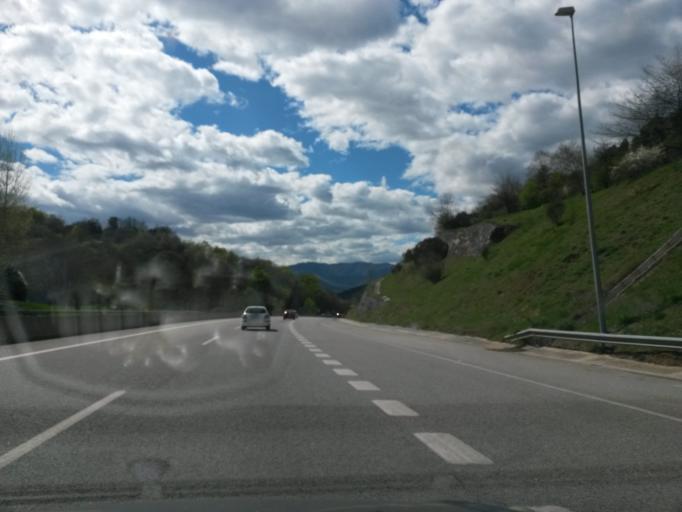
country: ES
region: Catalonia
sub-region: Provincia de Girona
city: Sant Joan les Fonts
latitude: 42.1927
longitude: 2.5219
